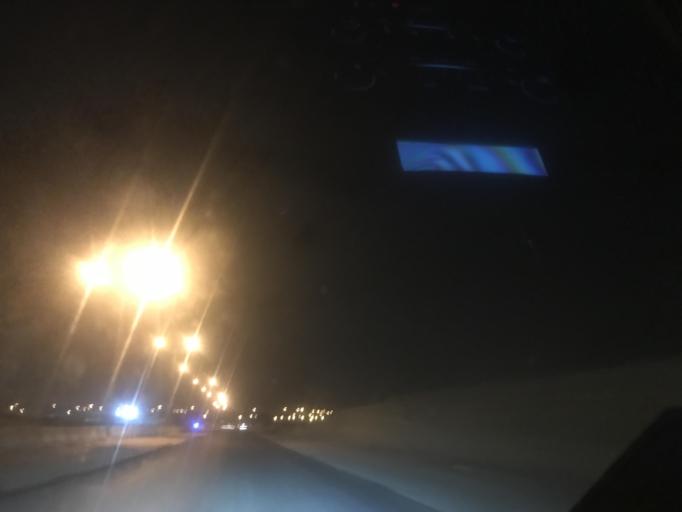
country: SA
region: Ar Riyad
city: Riyadh
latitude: 24.7610
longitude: 46.5889
